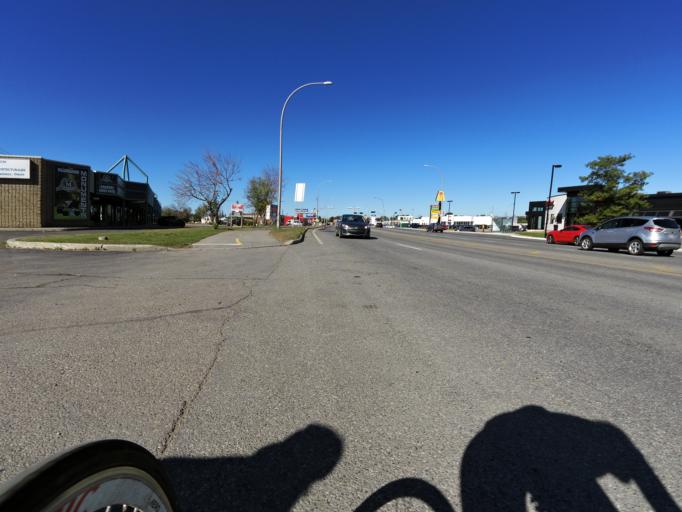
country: CA
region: Quebec
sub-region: Outaouais
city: Gatineau
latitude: 45.4834
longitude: -75.6610
